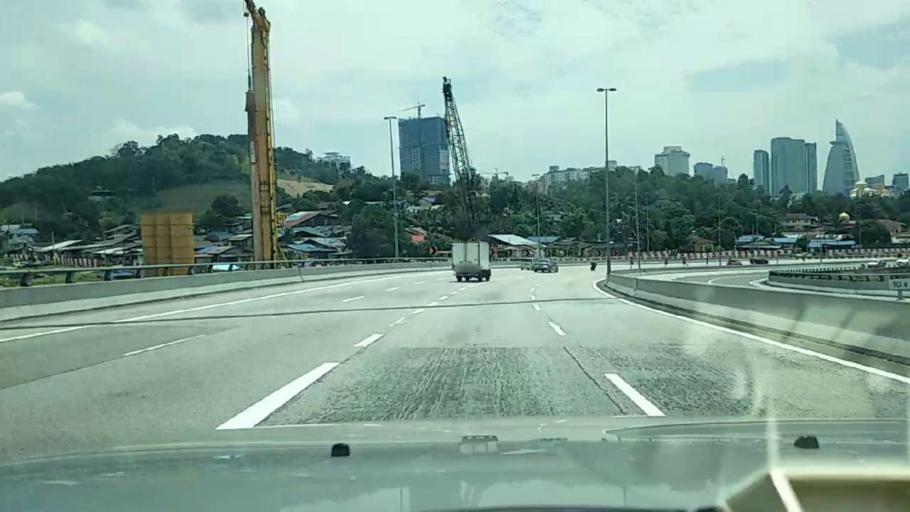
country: MY
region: Kuala Lumpur
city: Kuala Lumpur
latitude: 3.0946
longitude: 101.6697
